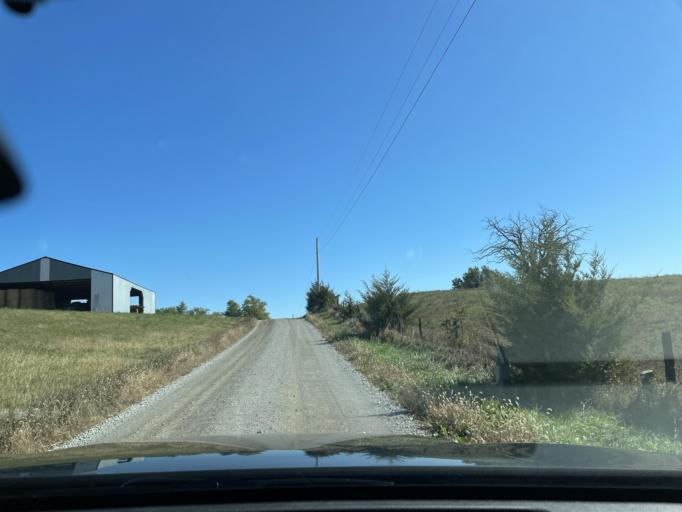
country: US
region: Missouri
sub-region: Andrew County
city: Savannah
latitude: 39.9393
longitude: -94.8768
